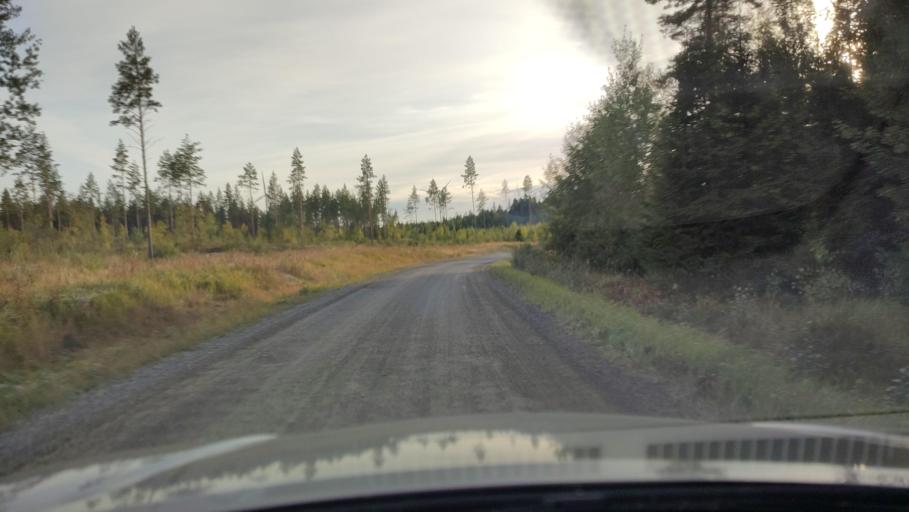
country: FI
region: Southern Ostrobothnia
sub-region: Suupohja
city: Karijoki
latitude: 62.1261
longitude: 21.6083
